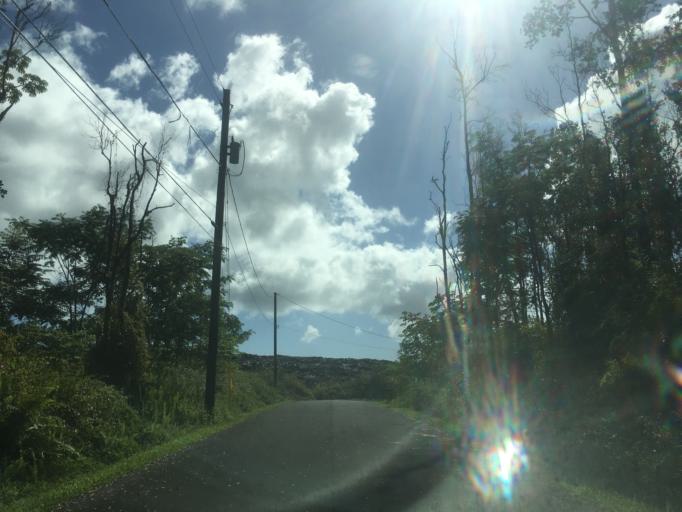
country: US
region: Hawaii
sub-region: Hawaii County
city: Leilani Estates
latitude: 19.4760
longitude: -154.9079
